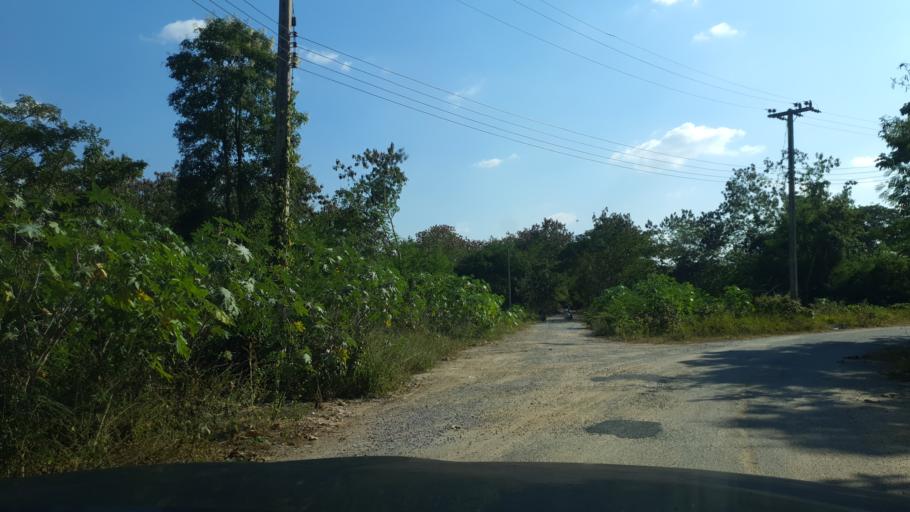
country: TH
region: Chiang Mai
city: Hang Dong
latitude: 18.7359
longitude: 98.9480
